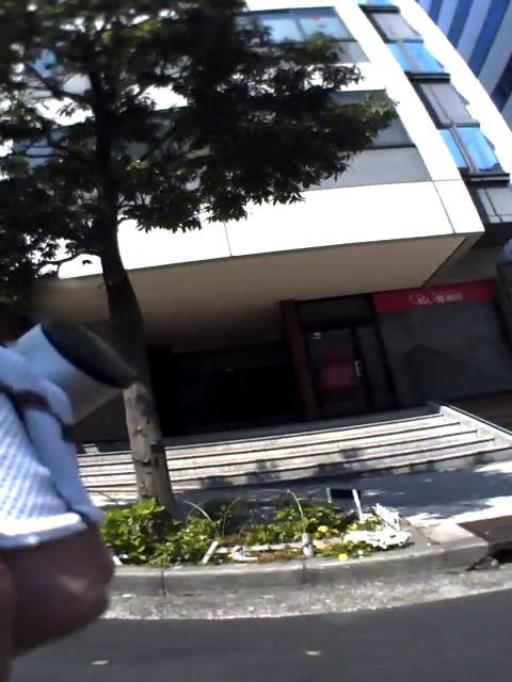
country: JP
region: Osaka
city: Osaka-shi
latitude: 34.6891
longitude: 135.5174
